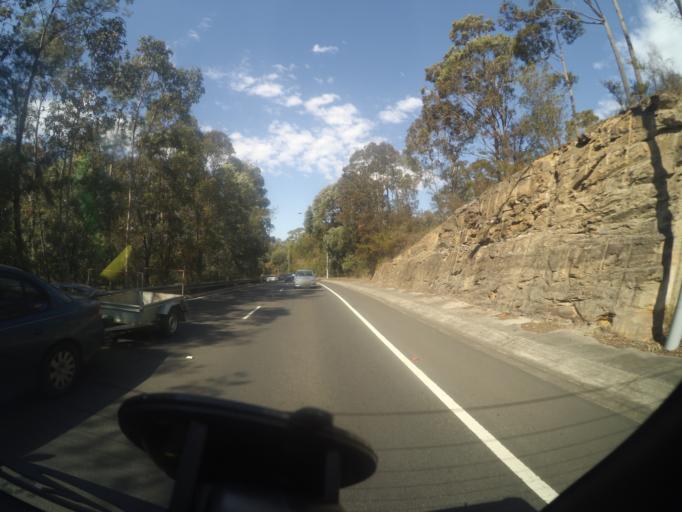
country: AU
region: New South Wales
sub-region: Blue Mountains Municipality
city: Blaxland
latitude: -33.7108
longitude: 150.5877
